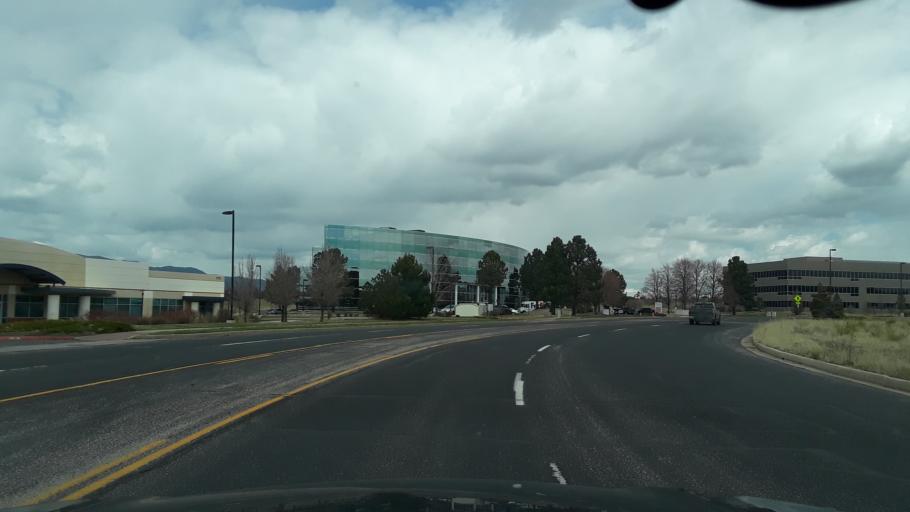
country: US
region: Colorado
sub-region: El Paso County
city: Air Force Academy
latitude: 38.9458
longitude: -104.8082
